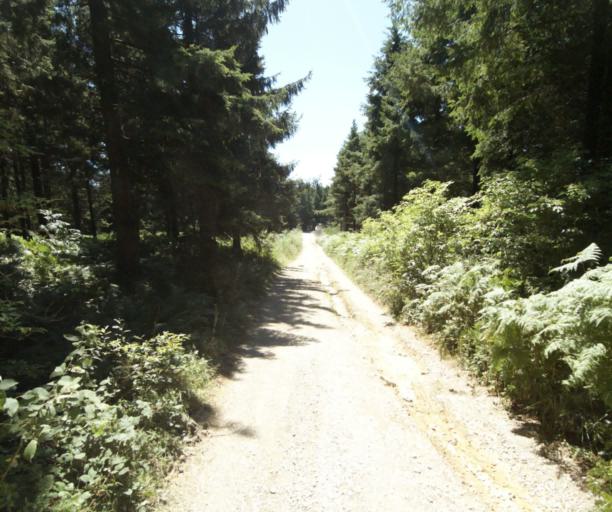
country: FR
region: Midi-Pyrenees
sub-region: Departement du Tarn
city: Dourgne
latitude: 43.4465
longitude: 2.1475
